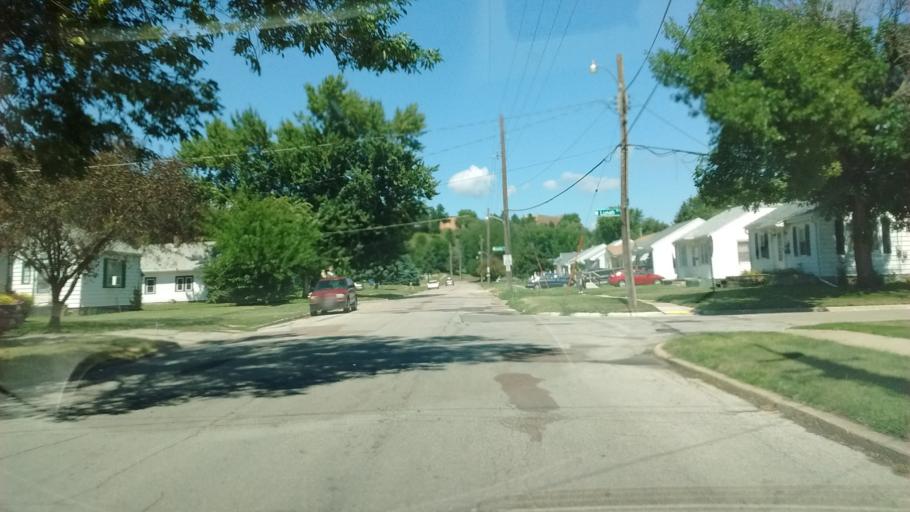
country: US
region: Iowa
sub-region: Woodbury County
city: Sioux City
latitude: 42.5221
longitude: -96.4256
